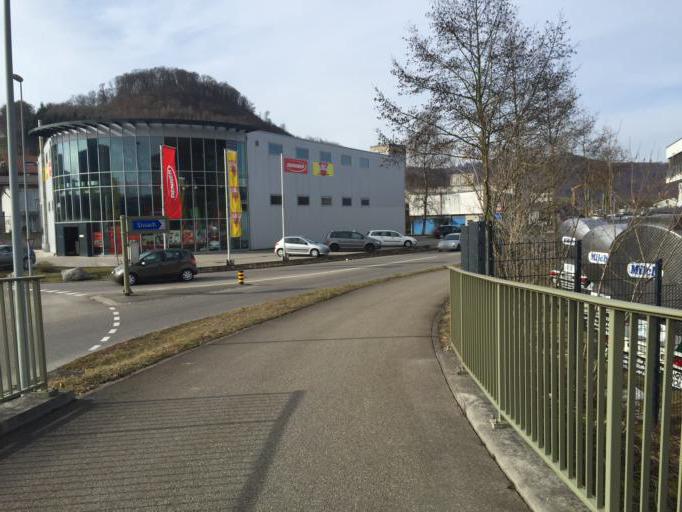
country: CH
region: Basel-Landschaft
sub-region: Bezirk Sissach
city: Sissach
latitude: 47.4623
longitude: 7.8249
